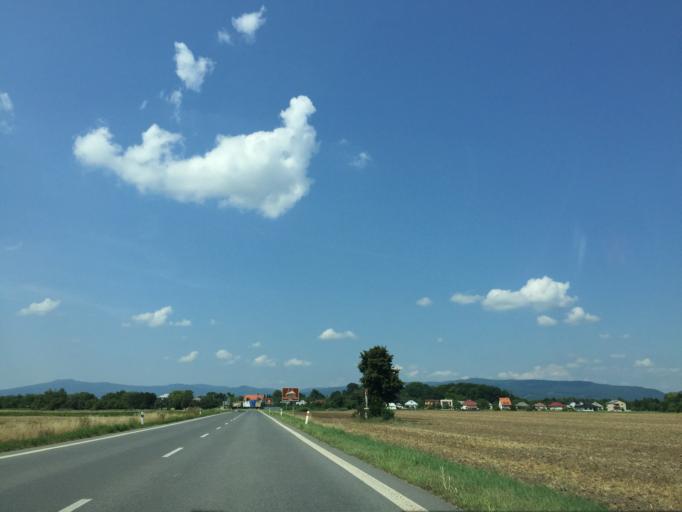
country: SK
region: Kosicky
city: Sobrance
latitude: 48.7325
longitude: 22.2111
